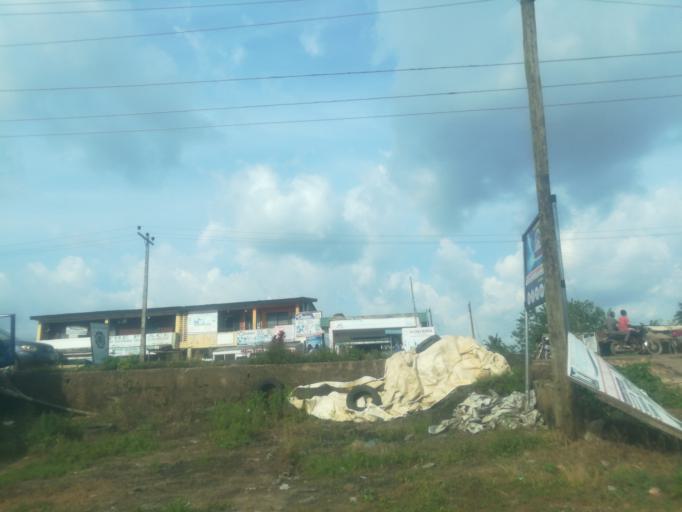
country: NG
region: Oyo
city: Ibadan
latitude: 7.3920
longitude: 3.8143
